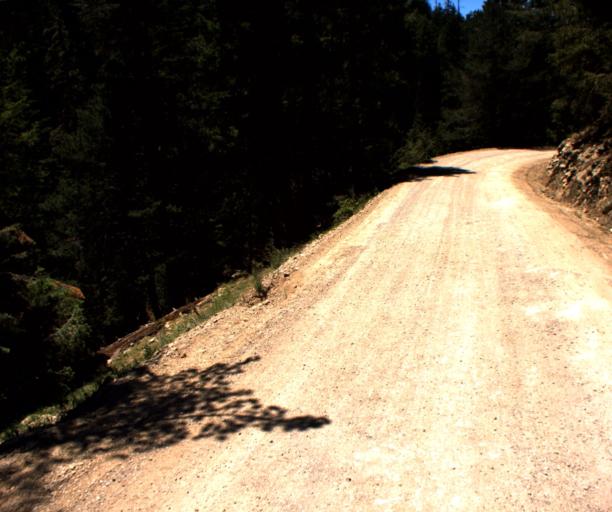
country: US
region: Arizona
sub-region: Graham County
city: Swift Trail Junction
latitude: 32.6727
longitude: -109.8865
